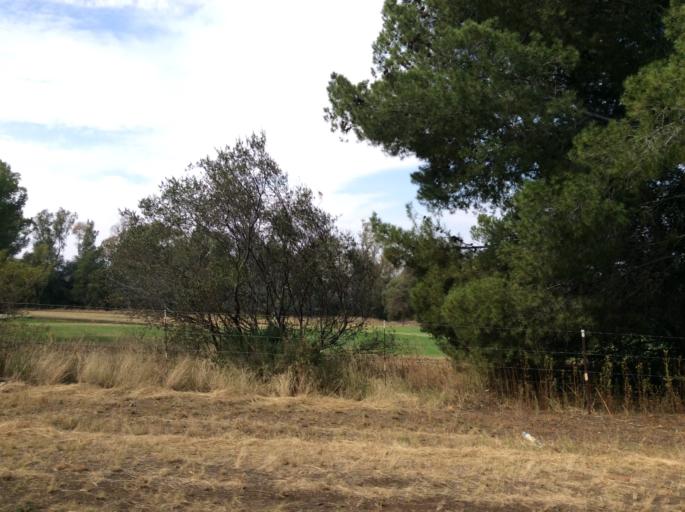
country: ZA
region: Orange Free State
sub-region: Xhariep District Municipality
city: Dewetsdorp
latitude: -29.5724
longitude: 26.6654
